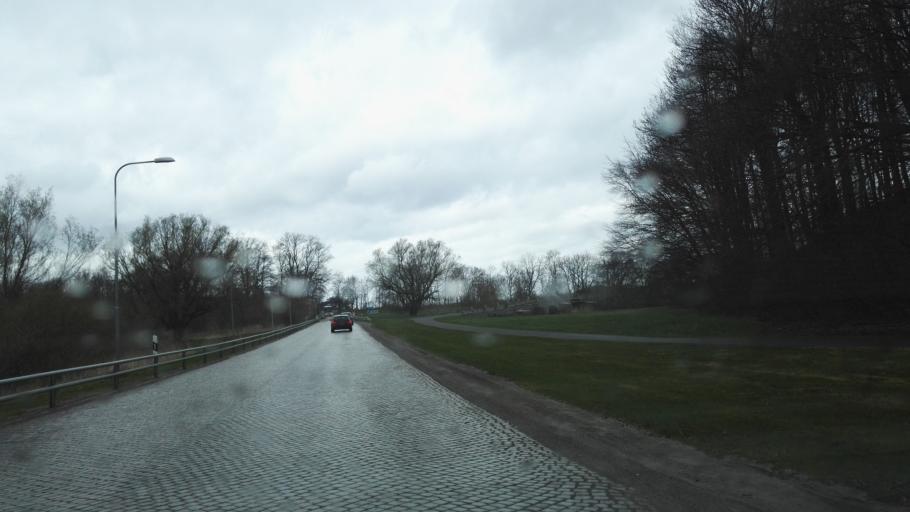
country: SE
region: Skane
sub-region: Simrishamns Kommun
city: Simrishamn
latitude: 55.5687
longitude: 14.3338
